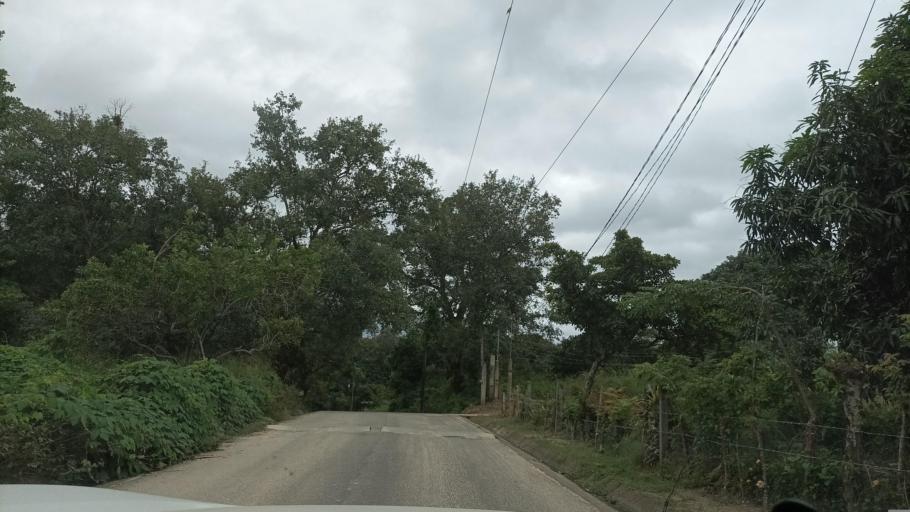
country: MX
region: Veracruz
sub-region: Cosoleacaque
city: Coacotla
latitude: 17.9494
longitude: -94.7111
